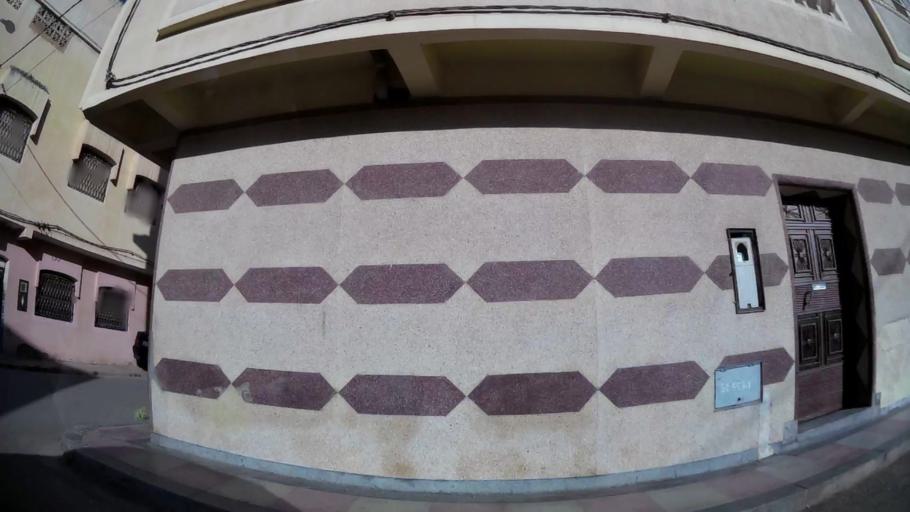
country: MA
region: Oriental
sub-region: Oujda-Angad
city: Oujda
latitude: 34.6798
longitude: -1.9380
